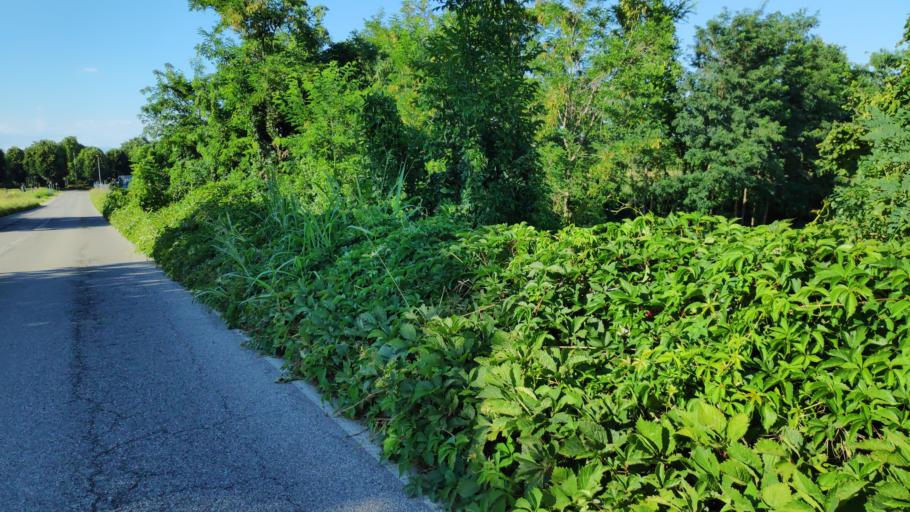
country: IT
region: Lombardy
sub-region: Citta metropolitana di Milano
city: Pozzuolo Martesana
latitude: 45.5110
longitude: 9.4604
